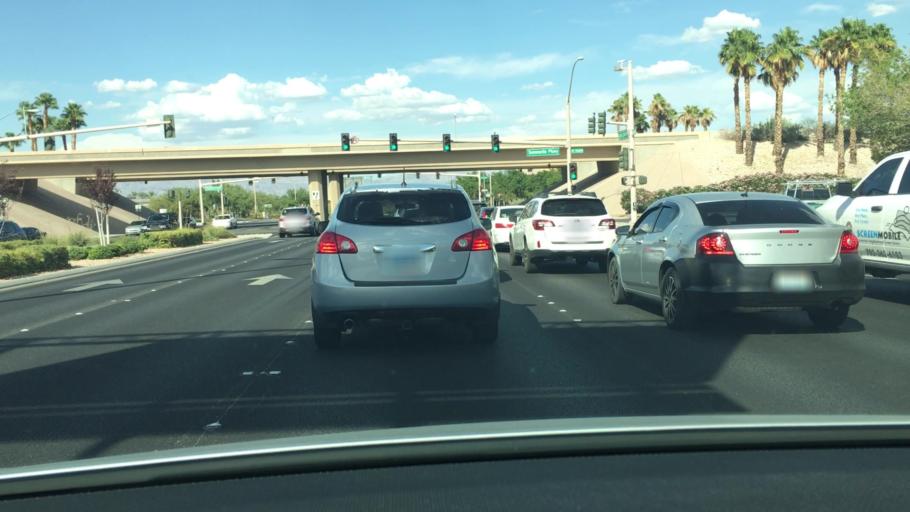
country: US
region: Nevada
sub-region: Clark County
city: Summerlin South
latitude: 36.1846
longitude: -115.3074
